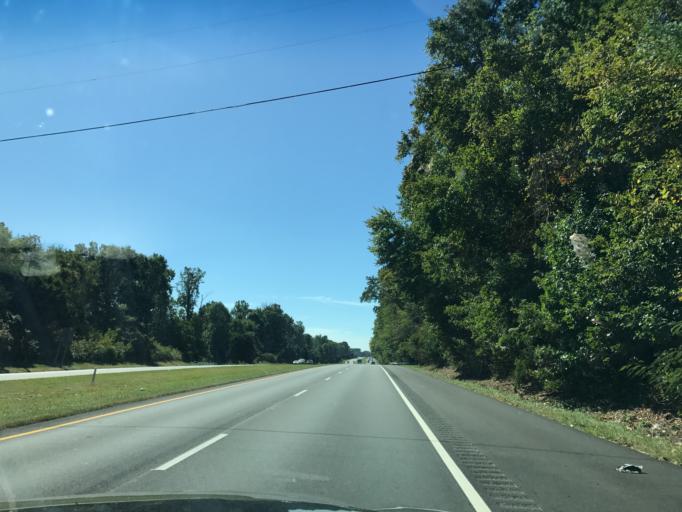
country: US
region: Virginia
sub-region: King George County
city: Dahlgren
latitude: 38.3922
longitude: -76.9547
